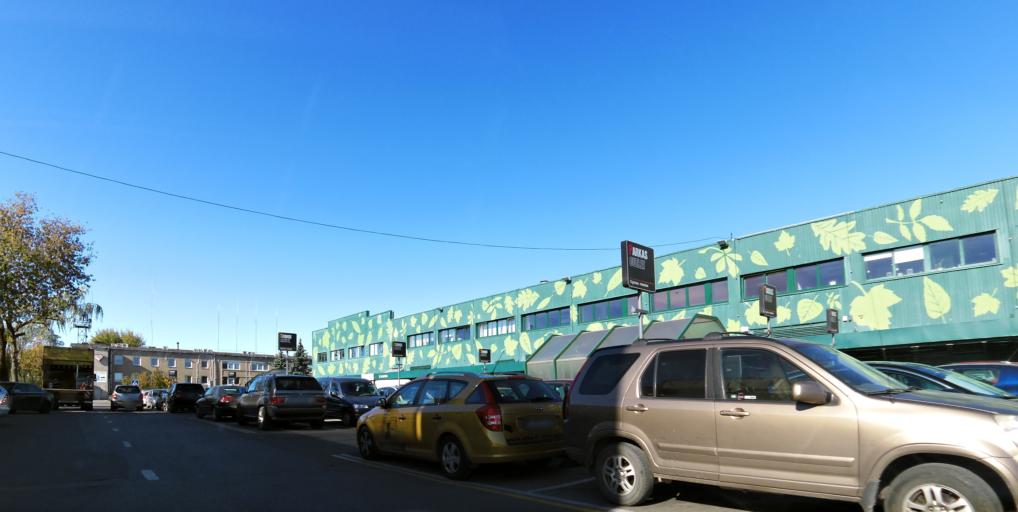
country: LT
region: Vilnius County
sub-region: Vilnius
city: Vilnius
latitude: 54.7138
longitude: 25.2976
